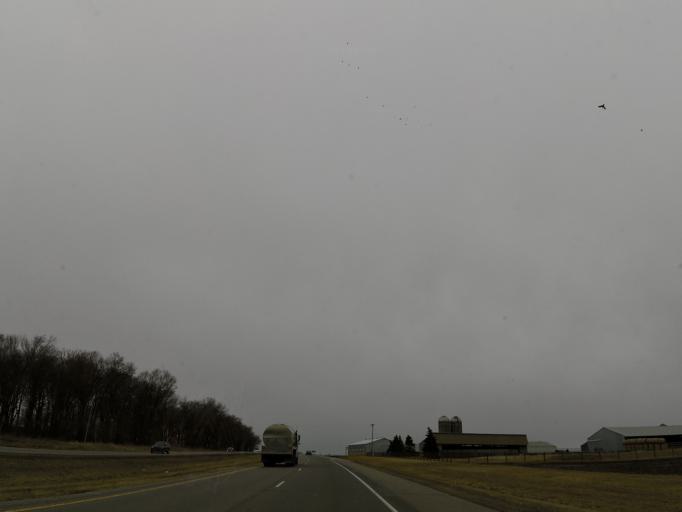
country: US
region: Minnesota
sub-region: Le Sueur County
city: Le Sueur
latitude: 44.5352
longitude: -93.8467
